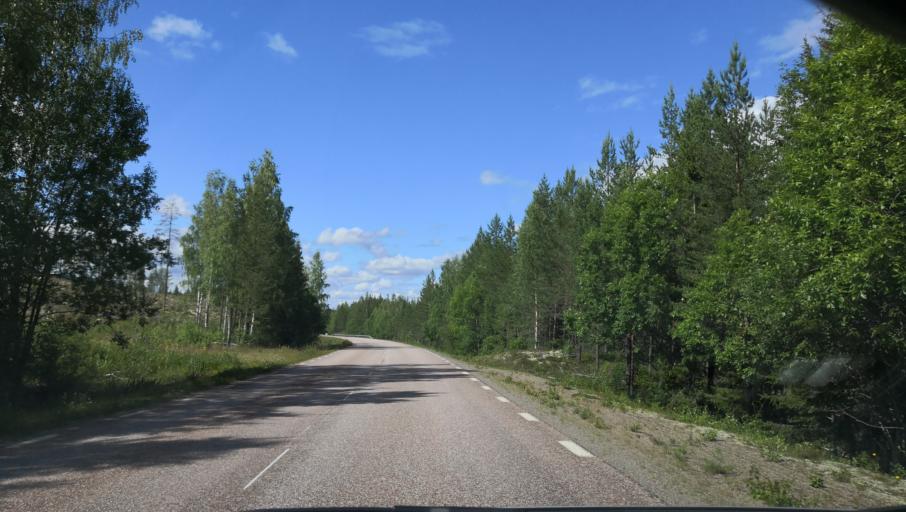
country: NO
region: Hedmark
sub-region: Trysil
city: Innbygda
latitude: 61.7154
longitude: 13.0059
